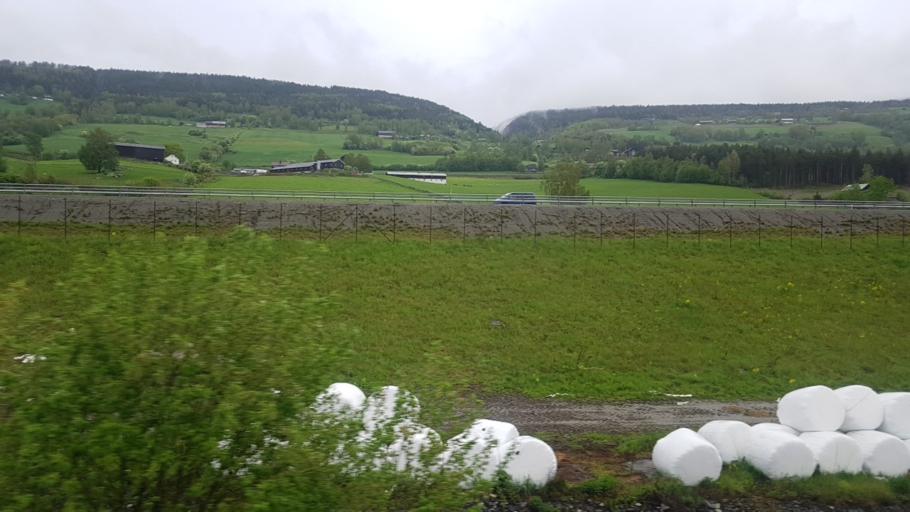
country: NO
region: Oppland
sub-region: Sor-Fron
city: Hundorp
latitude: 61.5705
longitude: 9.8706
